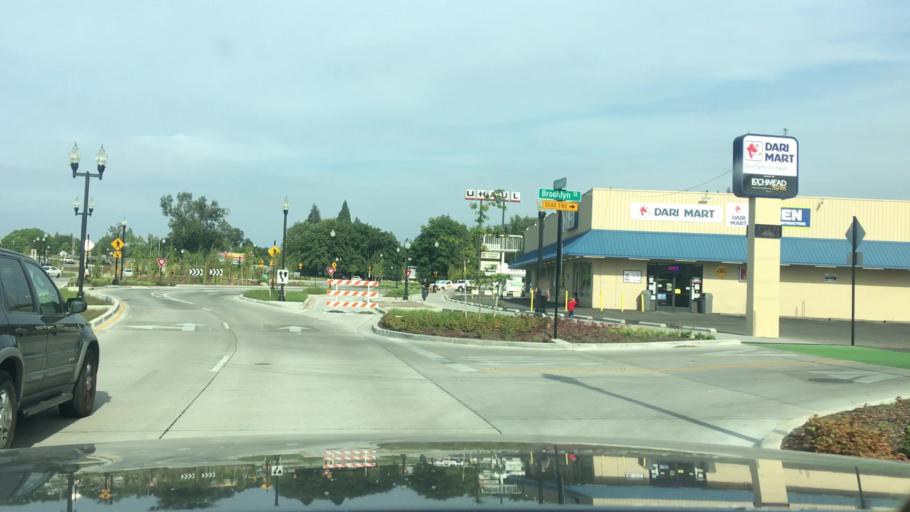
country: US
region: Oregon
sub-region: Lane County
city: Springfield
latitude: 44.0443
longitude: -123.0328
